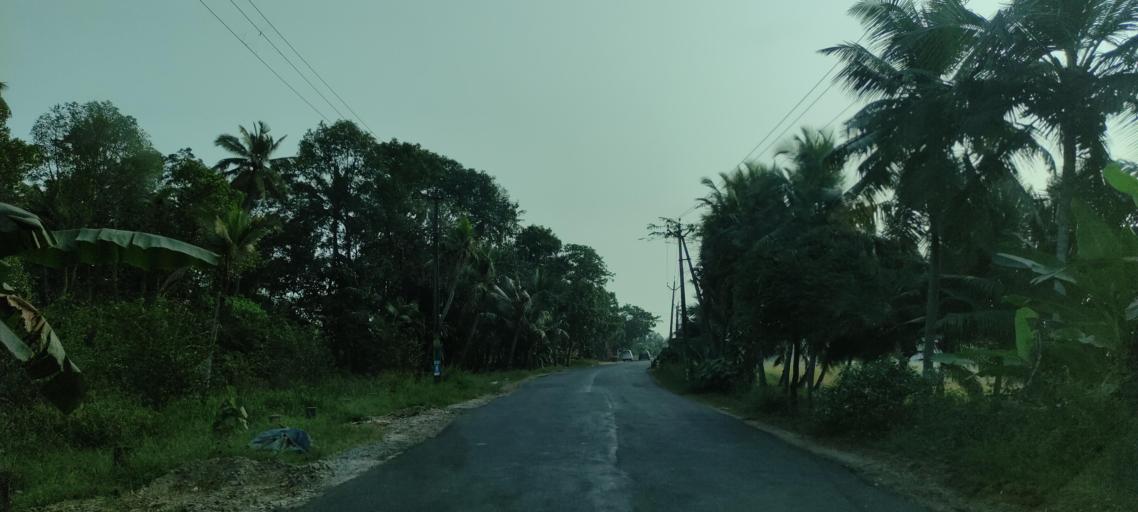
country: IN
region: Kerala
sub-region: Kottayam
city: Vaikam
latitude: 9.6878
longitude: 76.4639
